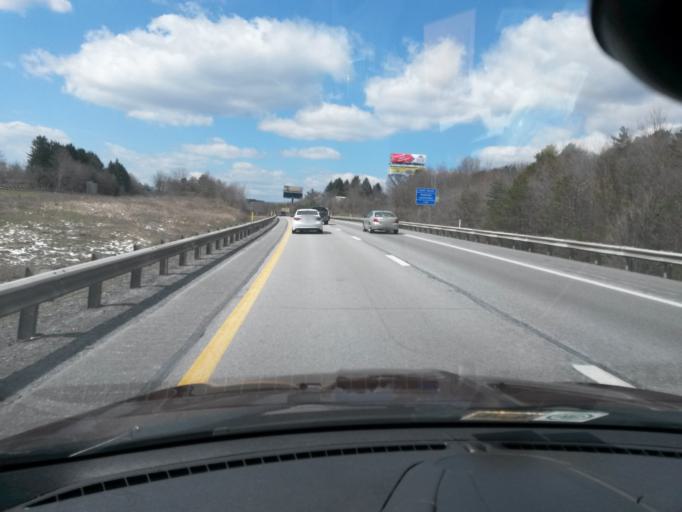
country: US
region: West Virginia
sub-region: Mercer County
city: Athens
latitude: 37.3815
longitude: -81.0453
